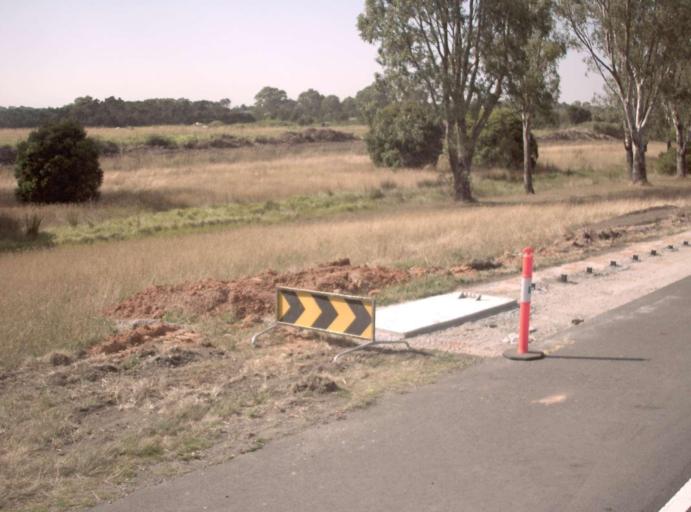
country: AU
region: Victoria
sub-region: Casey
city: Hallam
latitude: -38.0154
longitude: 145.2497
